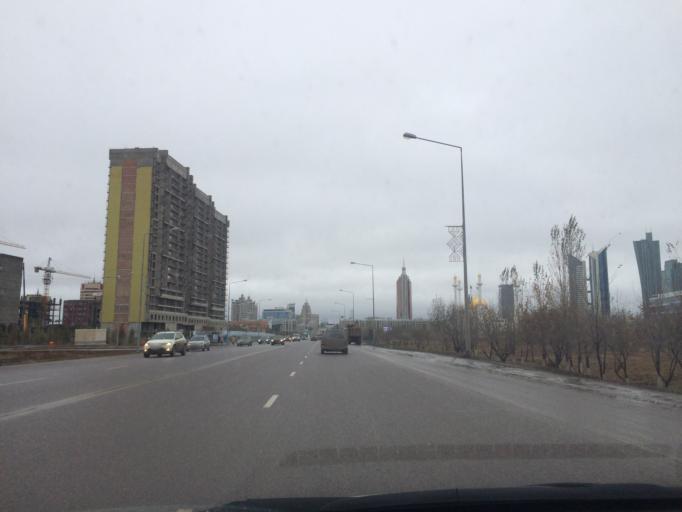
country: KZ
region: Astana Qalasy
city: Astana
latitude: 51.1215
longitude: 71.4124
